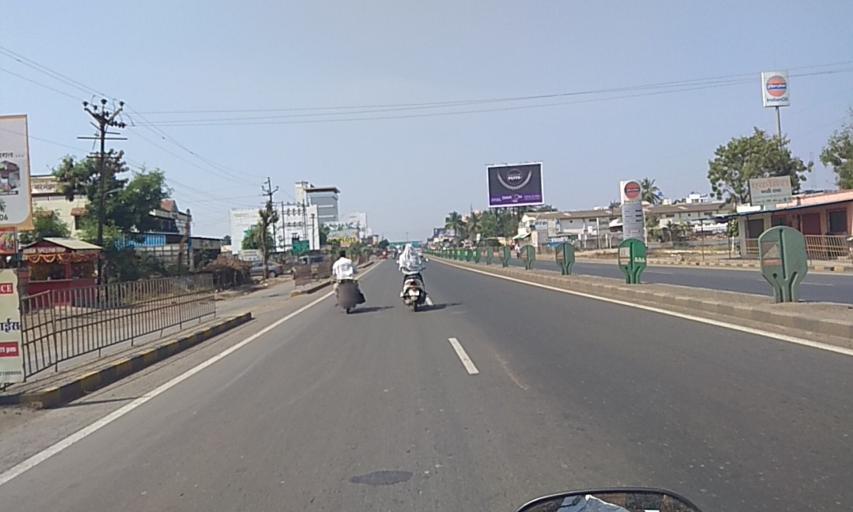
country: IN
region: Maharashtra
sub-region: Pune Division
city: Lohogaon
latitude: 18.4924
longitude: 73.9982
